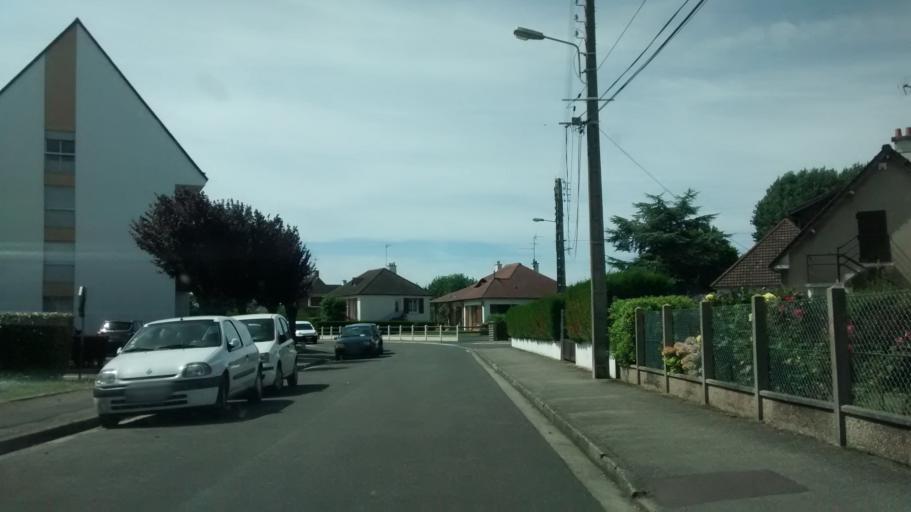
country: FR
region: Lower Normandy
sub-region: Departement du Calvados
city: Ouistreham
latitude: 49.2796
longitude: -0.2527
